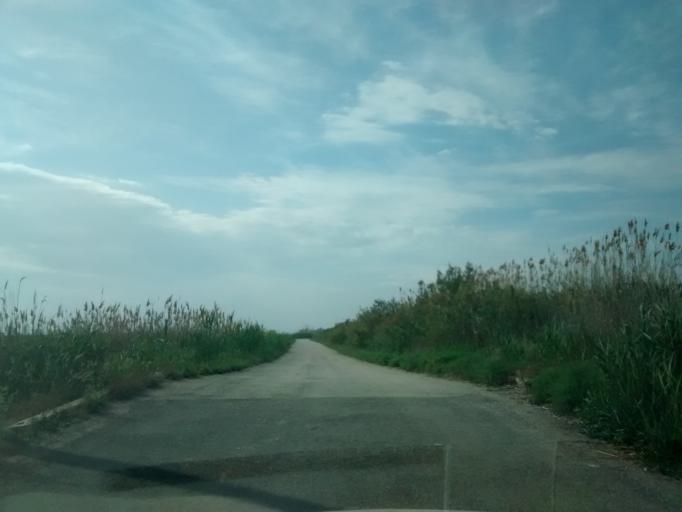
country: ES
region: Catalonia
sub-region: Provincia de Tarragona
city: Deltebre
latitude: 40.6882
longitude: 0.8481
